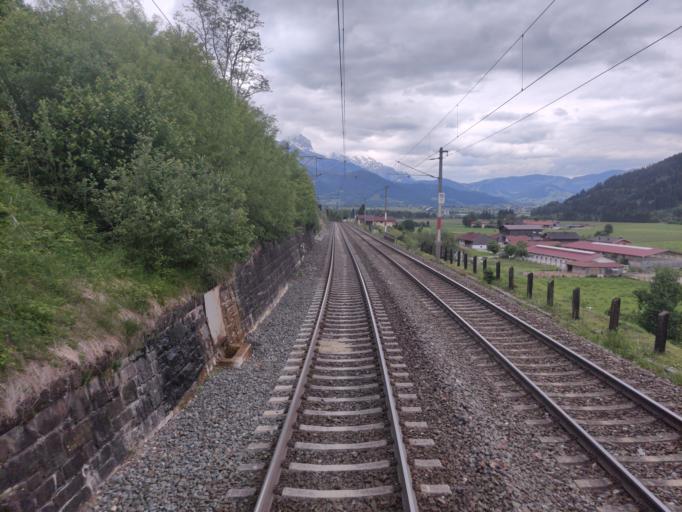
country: AT
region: Salzburg
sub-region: Politischer Bezirk Zell am See
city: Leogang
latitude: 47.4459
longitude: 12.7868
